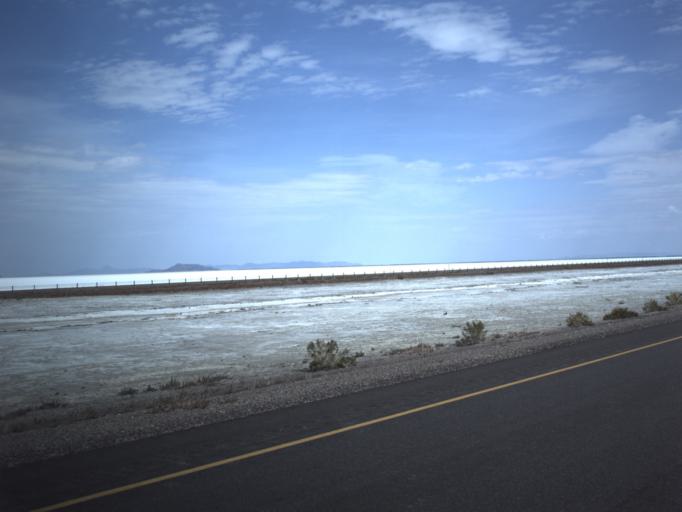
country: US
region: Utah
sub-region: Tooele County
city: Wendover
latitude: 40.7388
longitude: -113.8669
